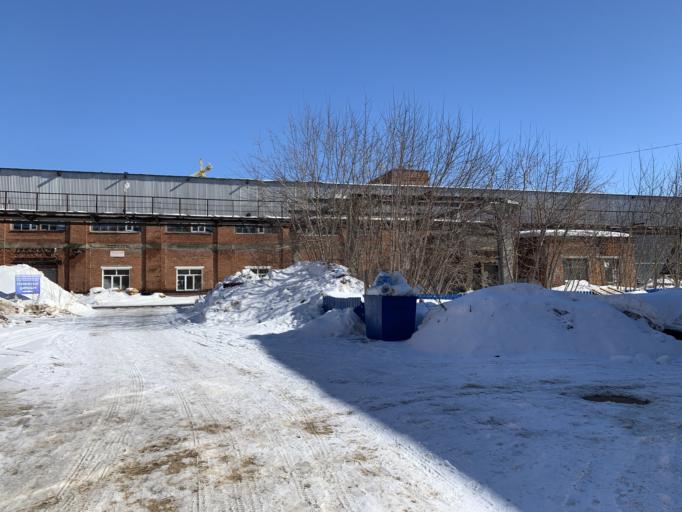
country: RU
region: Chuvashia
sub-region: Cheboksarskiy Rayon
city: Cheboksary
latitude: 56.1450
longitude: 47.2780
